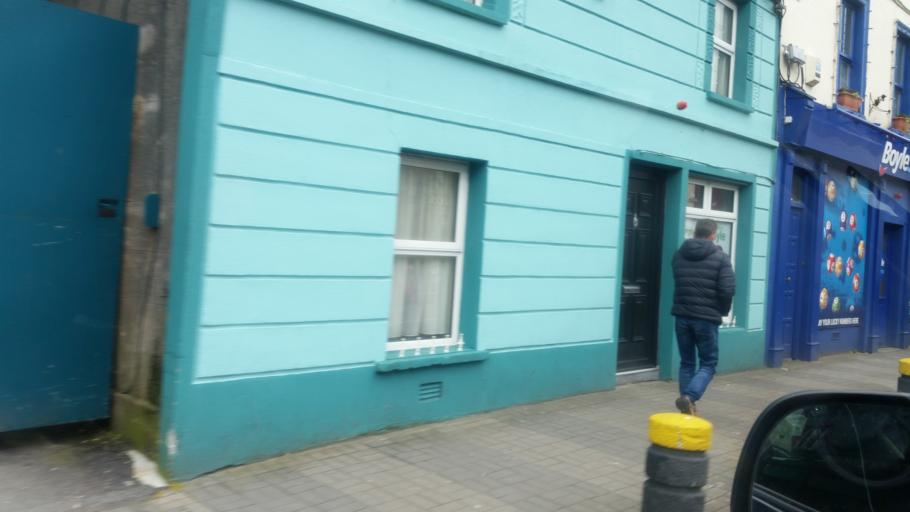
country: IE
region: Leinster
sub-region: Kildare
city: Kildare
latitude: 53.1570
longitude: -6.9116
